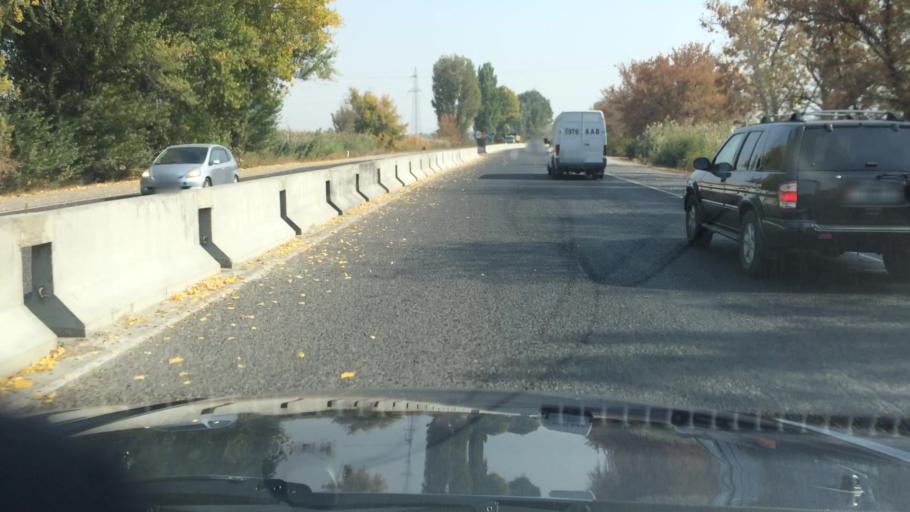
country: KG
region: Chuy
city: Kant
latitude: 42.9760
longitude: 74.8817
